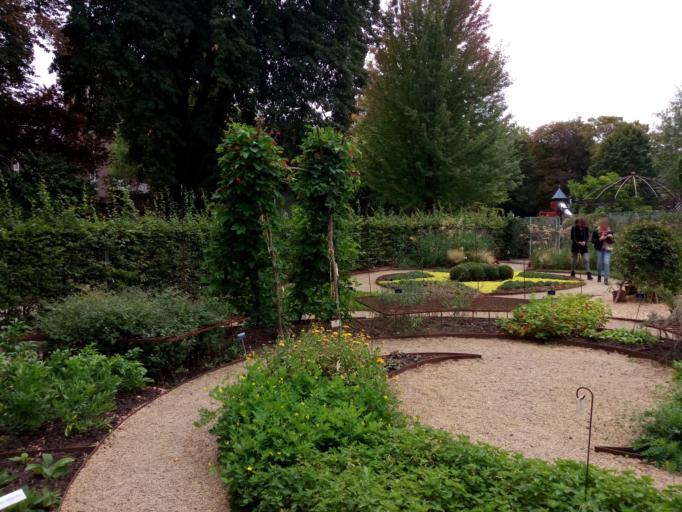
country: BE
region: Wallonia
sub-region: Province de Namur
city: Namur
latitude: 50.4660
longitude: 4.8577
